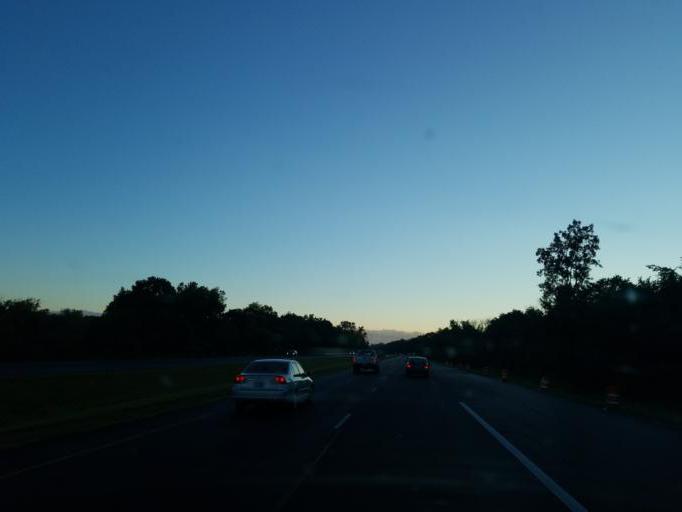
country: US
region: Ohio
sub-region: Summit County
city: Norton
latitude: 41.0827
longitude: -81.6631
